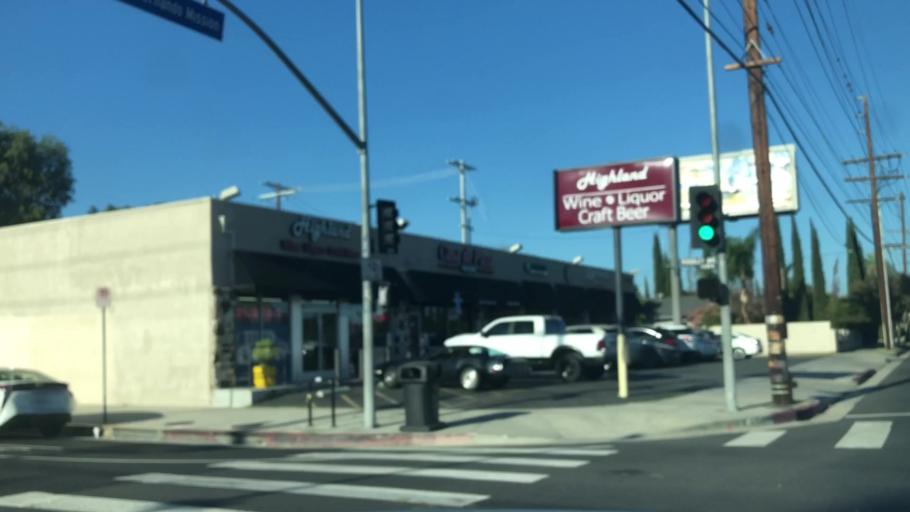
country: US
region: California
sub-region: Los Angeles County
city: San Fernando
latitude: 34.2720
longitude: -118.4848
